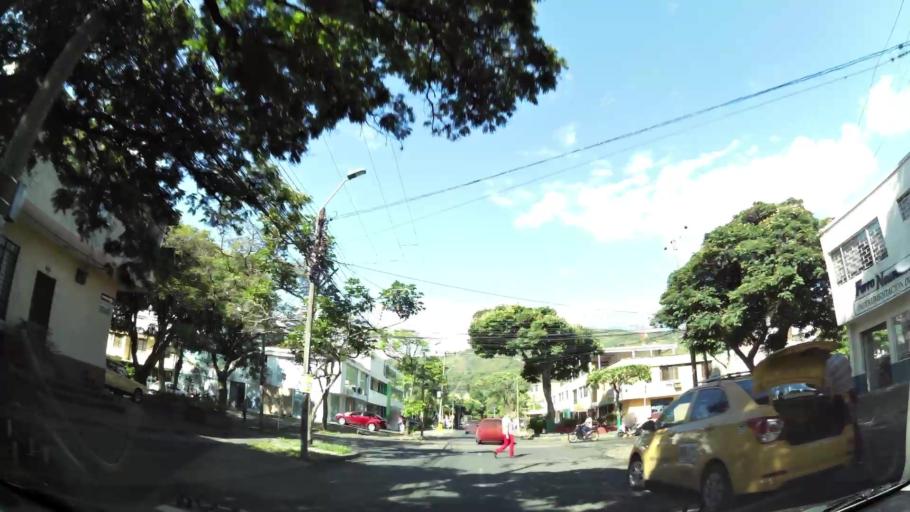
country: CO
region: Valle del Cauca
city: Cali
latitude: 3.4688
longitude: -76.5258
